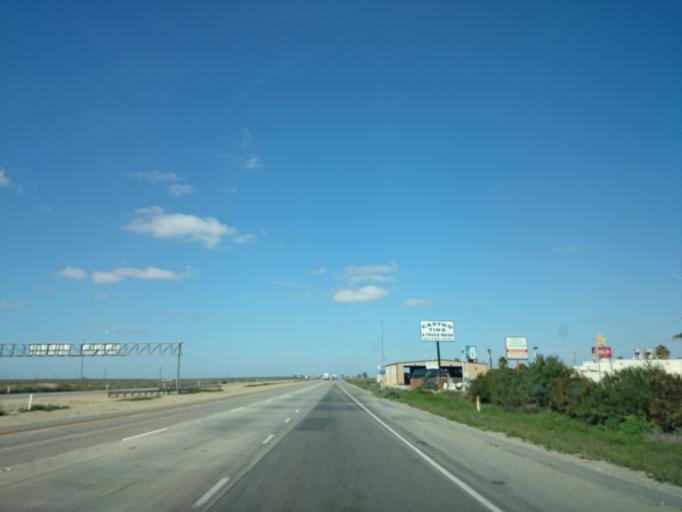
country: US
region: California
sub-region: Kern County
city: Buttonwillow
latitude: 35.4015
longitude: -119.4005
